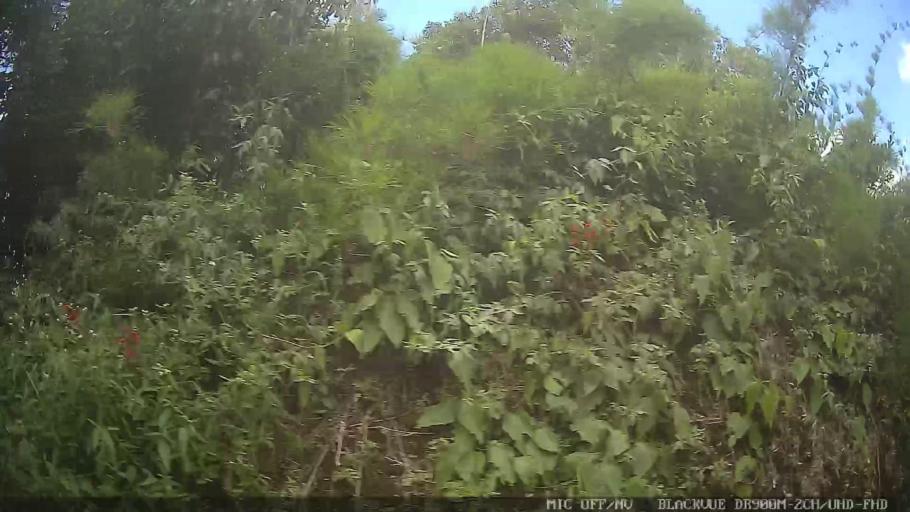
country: BR
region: Minas Gerais
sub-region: Extrema
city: Extrema
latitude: -22.8888
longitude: -46.3193
